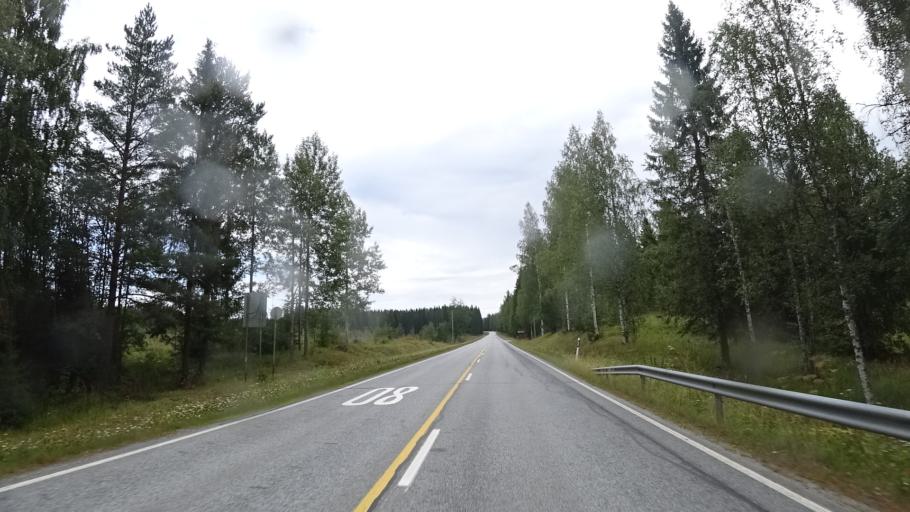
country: FI
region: North Karelia
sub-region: Keski-Karjala
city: Raeaekkylae
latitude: 62.1064
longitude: 29.6886
